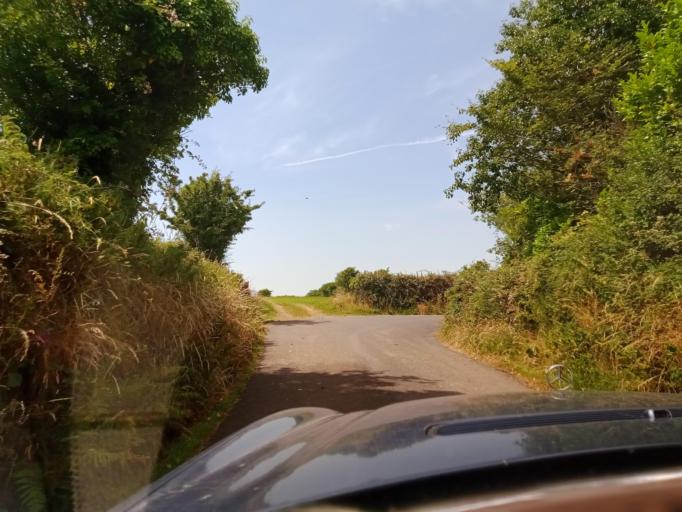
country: IE
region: Leinster
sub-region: Kilkenny
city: Mooncoin
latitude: 52.2572
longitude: -7.2136
